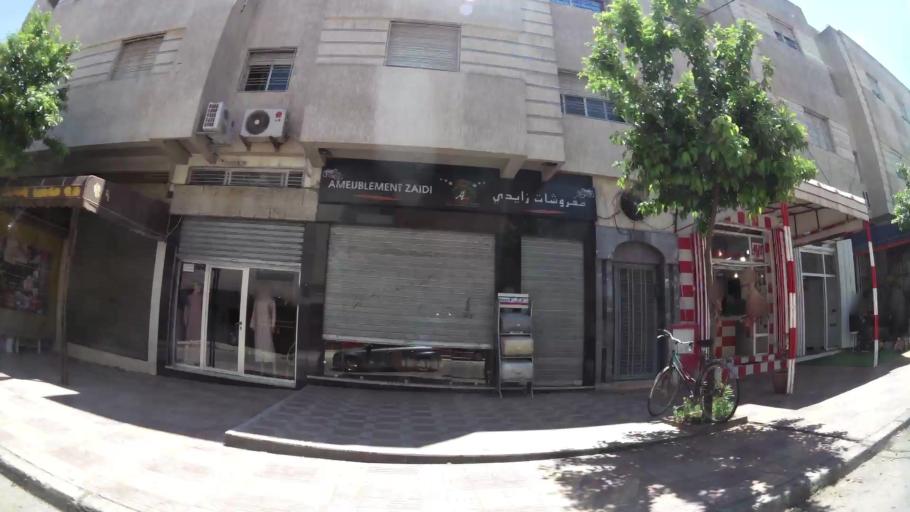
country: MA
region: Fes-Boulemane
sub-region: Fes
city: Fes
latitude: 34.0074
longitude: -4.9856
